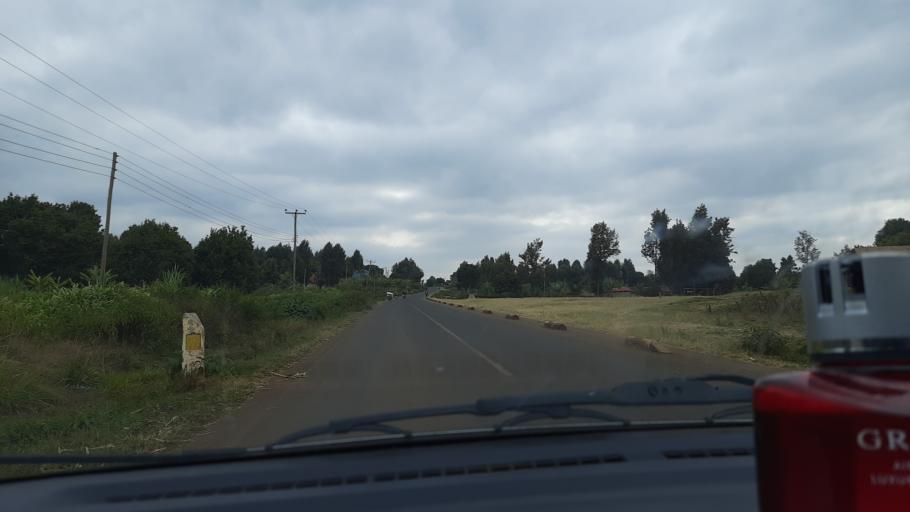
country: TZ
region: Kilimanjaro
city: Moshi
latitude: -2.9713
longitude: 37.5331
